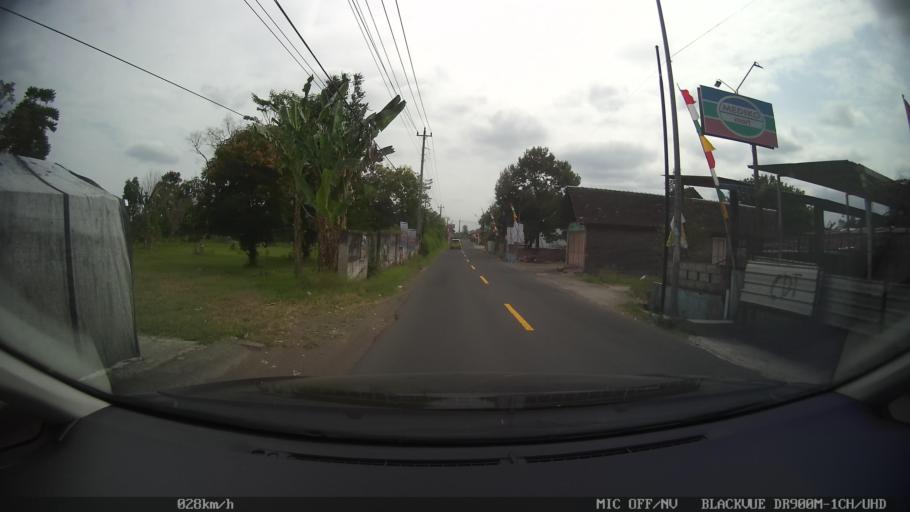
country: ID
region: Central Java
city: Candi Prambanan
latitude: -7.7364
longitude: 110.4803
